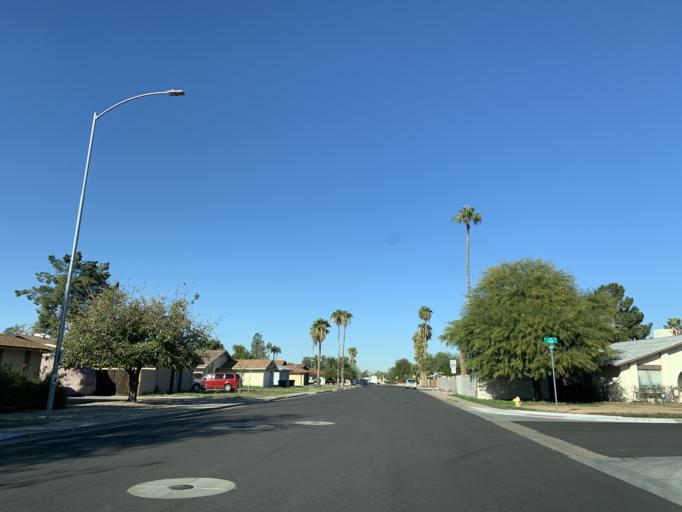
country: US
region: Arizona
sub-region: Maricopa County
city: Tempe
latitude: 33.3973
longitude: -111.8807
